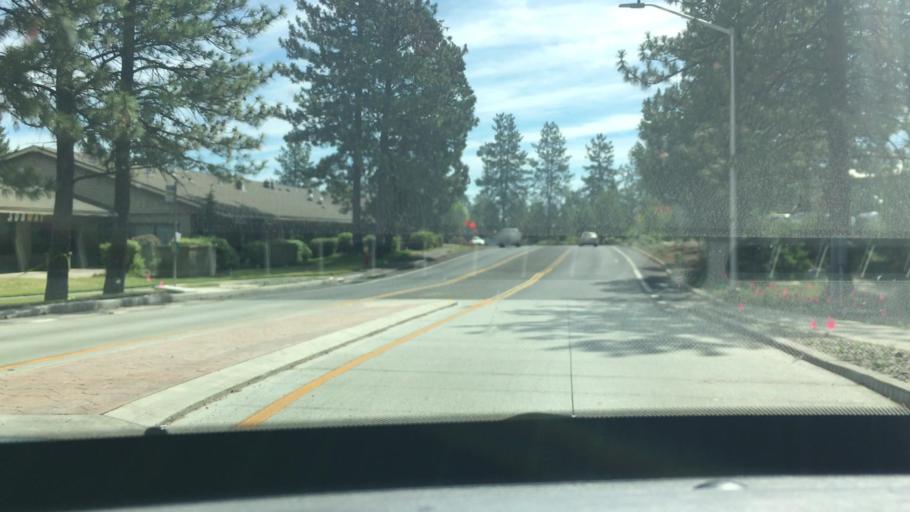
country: US
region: Oregon
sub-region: Deschutes County
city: Bend
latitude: 44.0478
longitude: -121.3314
